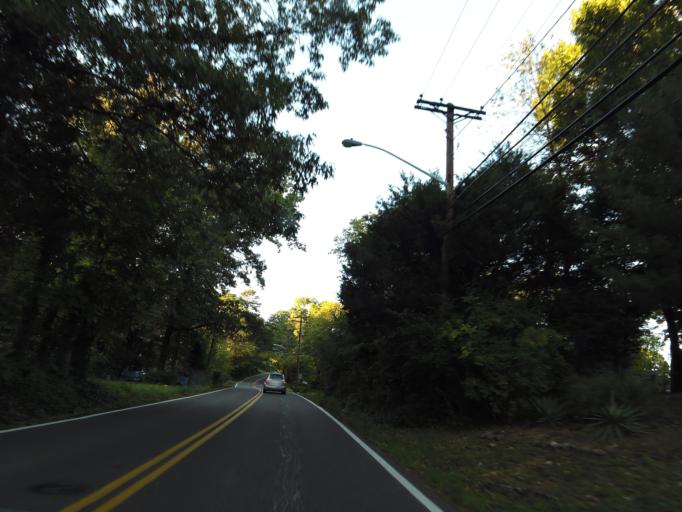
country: US
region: Tennessee
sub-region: Knox County
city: Knoxville
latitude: 36.0267
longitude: -83.9551
